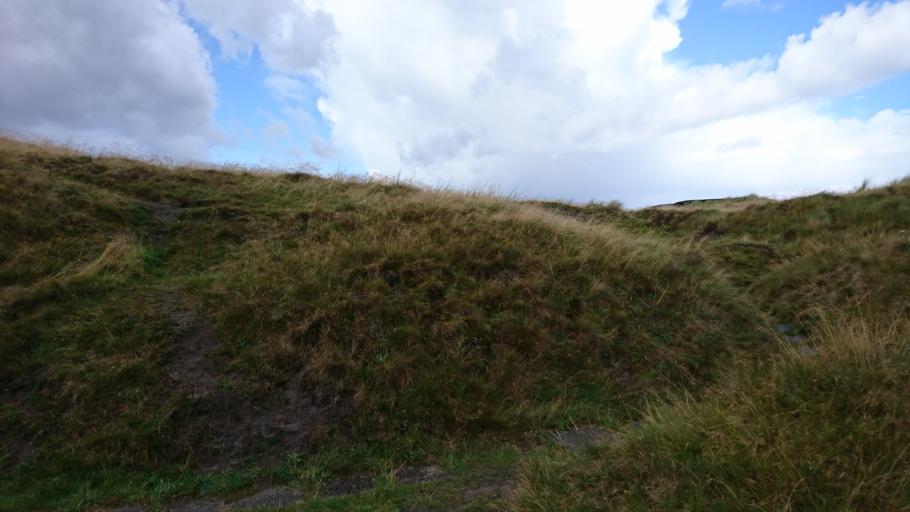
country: DK
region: South Denmark
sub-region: Fano Kommune
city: Nordby
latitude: 55.4608
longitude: 8.3972
